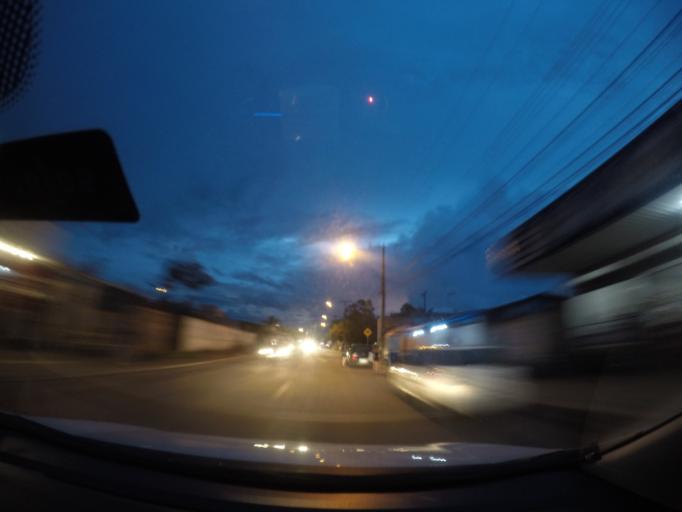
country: BR
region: Goias
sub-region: Goiania
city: Goiania
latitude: -16.7266
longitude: -49.3691
